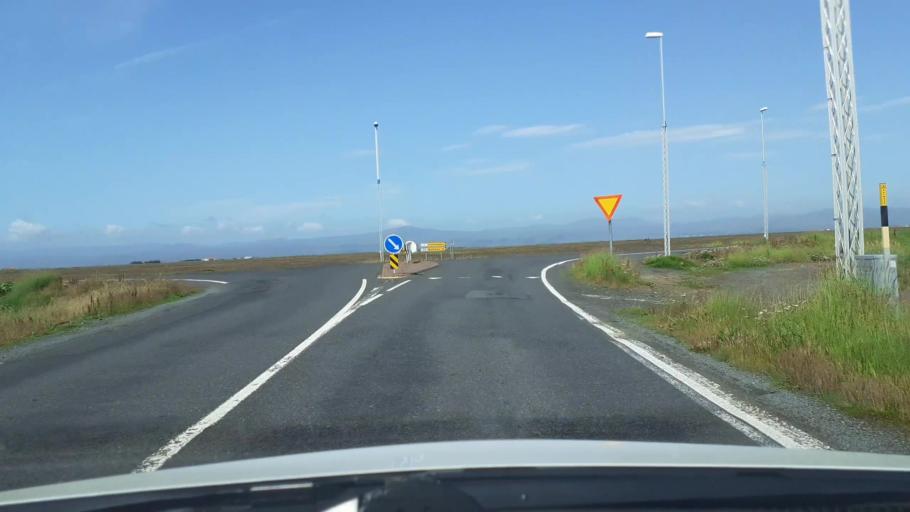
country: IS
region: South
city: Selfoss
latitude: 63.8602
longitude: -21.1098
